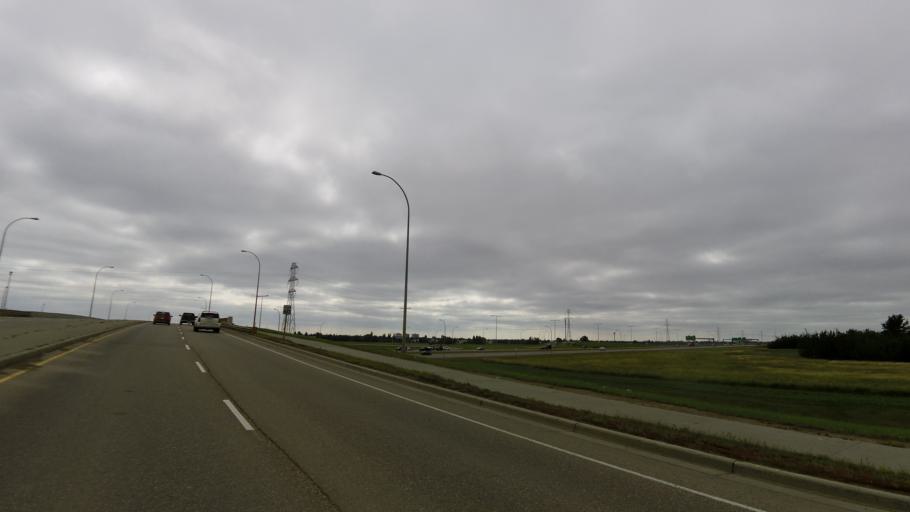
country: CA
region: Alberta
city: St. Albert
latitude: 53.5231
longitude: -113.6616
